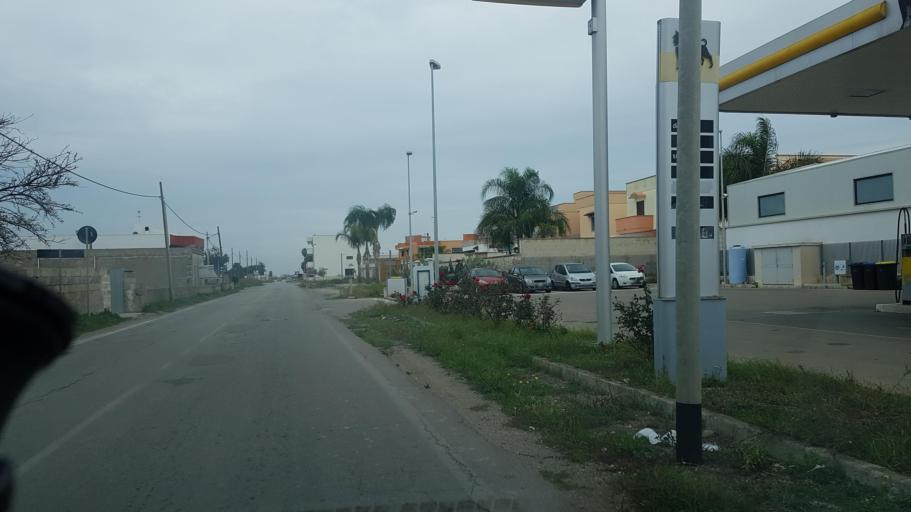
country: IT
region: Apulia
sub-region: Provincia di Lecce
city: Leverano
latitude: 40.2983
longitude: 17.9945
